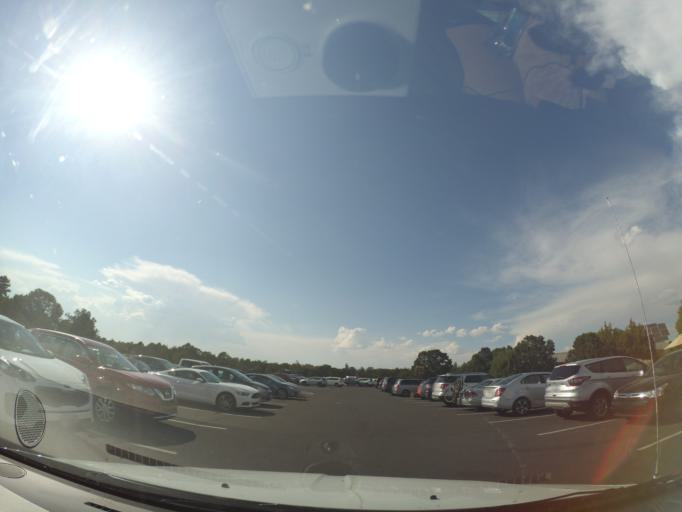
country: US
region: Arizona
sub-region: Coconino County
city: Grand Canyon
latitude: 36.0586
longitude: -112.1102
